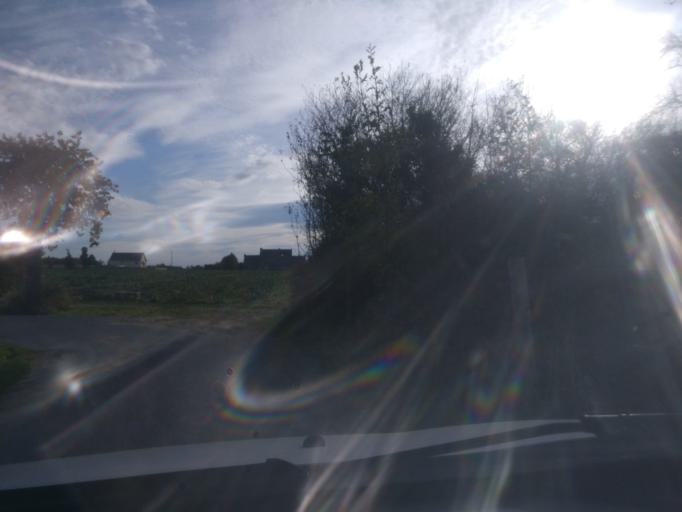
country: FR
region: Brittany
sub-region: Departement d'Ille-et-Vilaine
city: Cancale
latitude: 48.6772
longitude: -1.8722
